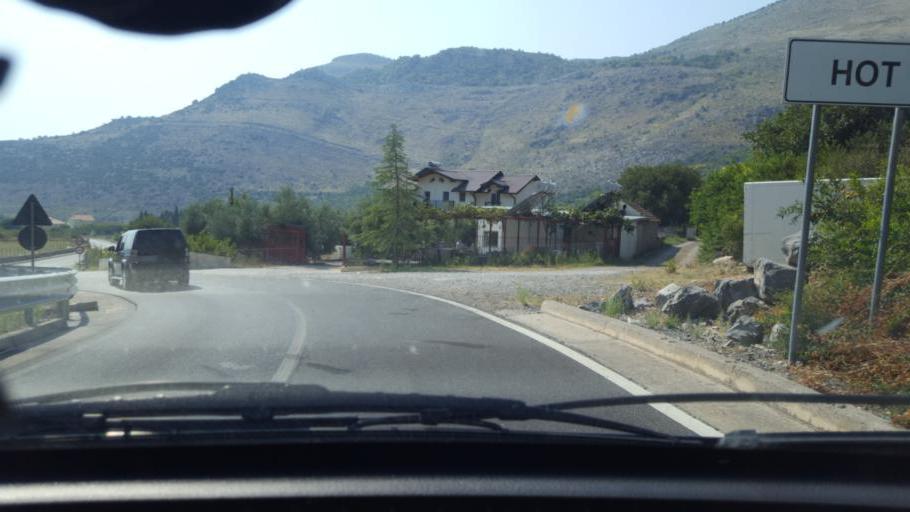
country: AL
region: Shkoder
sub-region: Rrethi i Malesia e Madhe
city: Hot
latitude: 42.3665
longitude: 19.4476
